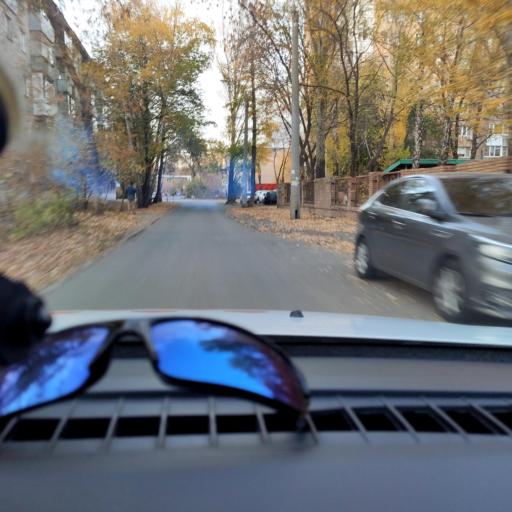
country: RU
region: Samara
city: Samara
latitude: 53.2030
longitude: 50.1859
